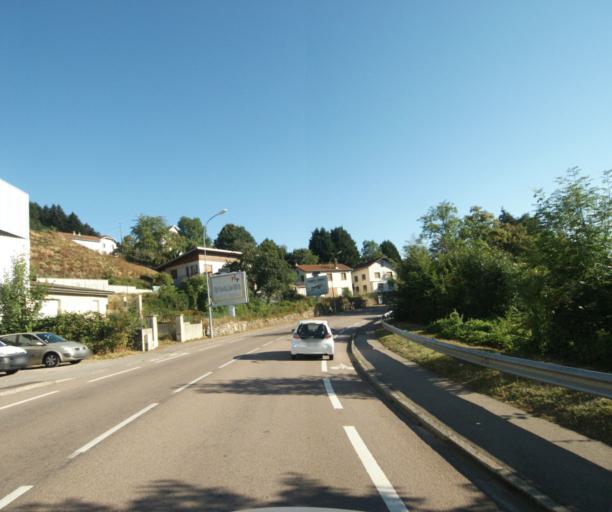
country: FR
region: Lorraine
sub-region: Departement des Vosges
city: Chantraine
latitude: 48.1537
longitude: 6.4497
